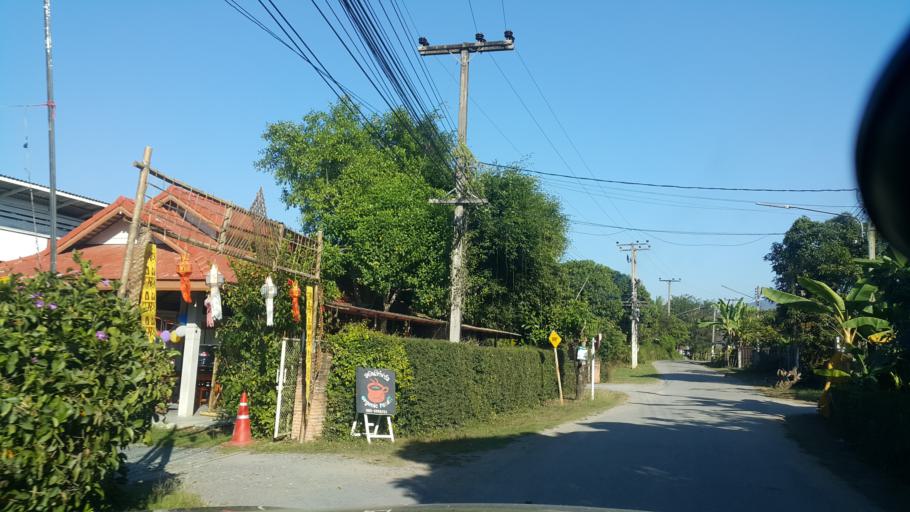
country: TH
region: Chiang Mai
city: Mae On
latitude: 18.7368
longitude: 99.2145
